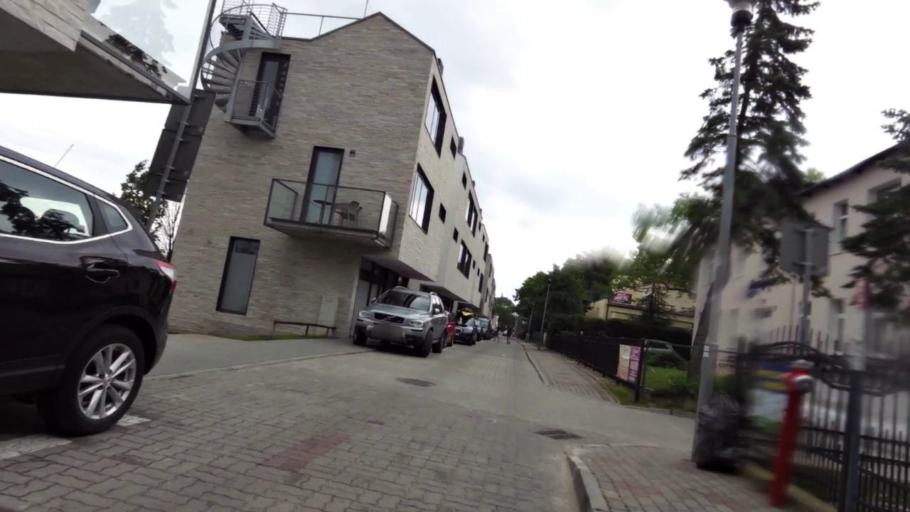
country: PL
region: West Pomeranian Voivodeship
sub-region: Powiat kolobrzeski
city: Ustronie Morskie
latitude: 54.2170
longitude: 15.7571
